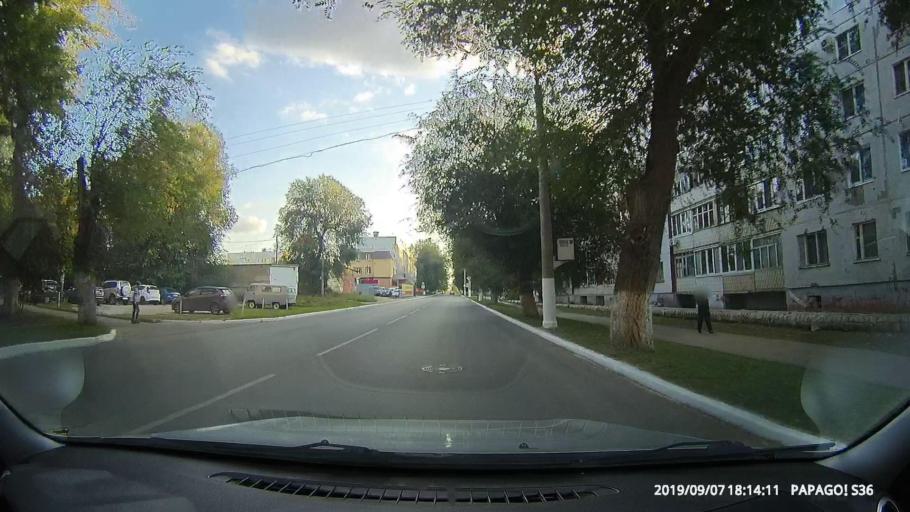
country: RU
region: Samara
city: Chapayevsk
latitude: 52.9972
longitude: 49.7749
